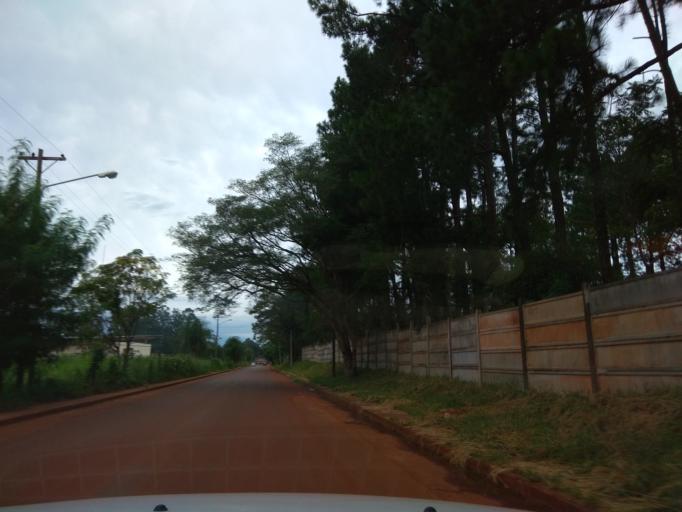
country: AR
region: Misiones
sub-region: Departamento de Capital
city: Posadas
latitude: -27.4386
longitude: -55.8901
